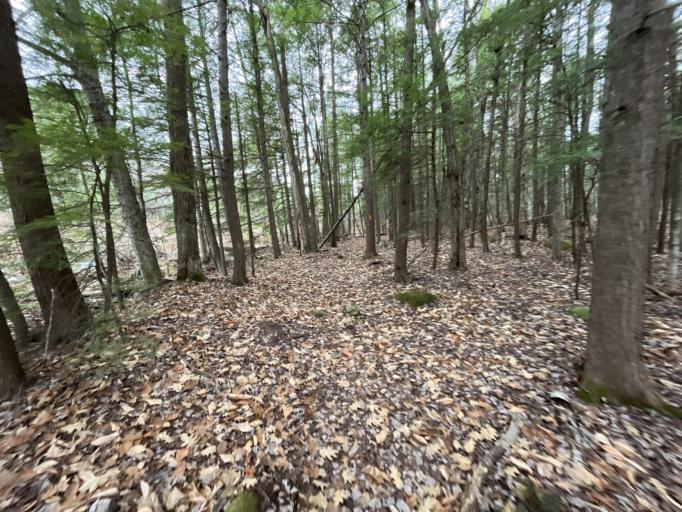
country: US
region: New Hampshire
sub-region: Merrimack County
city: New London
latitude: 43.3947
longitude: -71.9732
